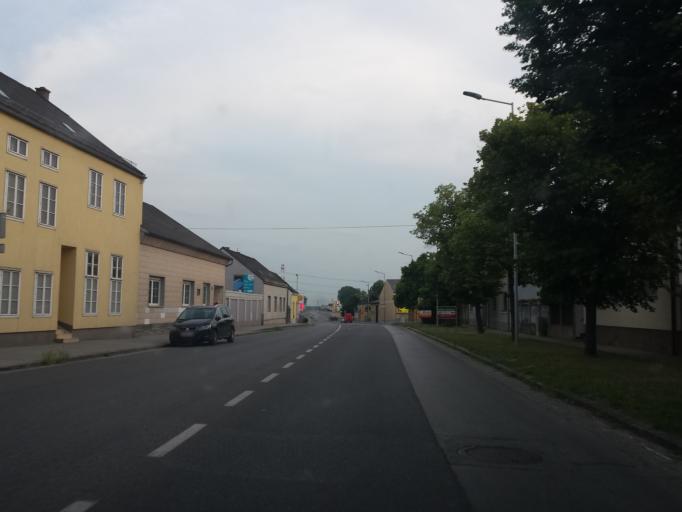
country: AT
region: Lower Austria
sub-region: Politischer Bezirk Ganserndorf
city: Deutsch-Wagram
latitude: 48.2967
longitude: 16.5601
